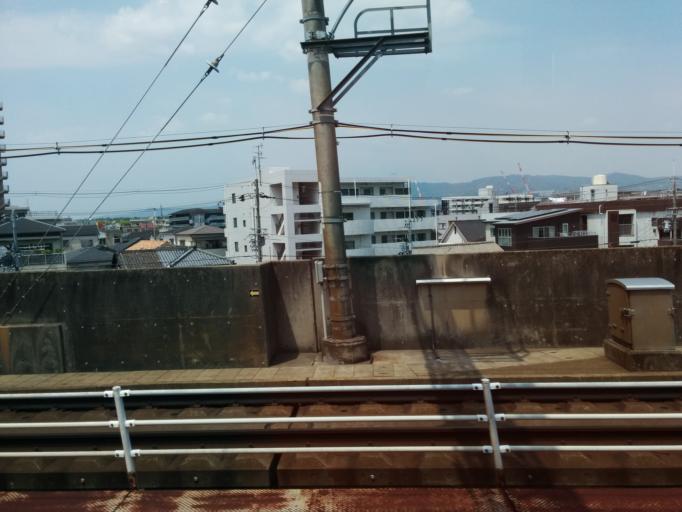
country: JP
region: Osaka
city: Ibaraki
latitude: 34.8192
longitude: 135.5781
